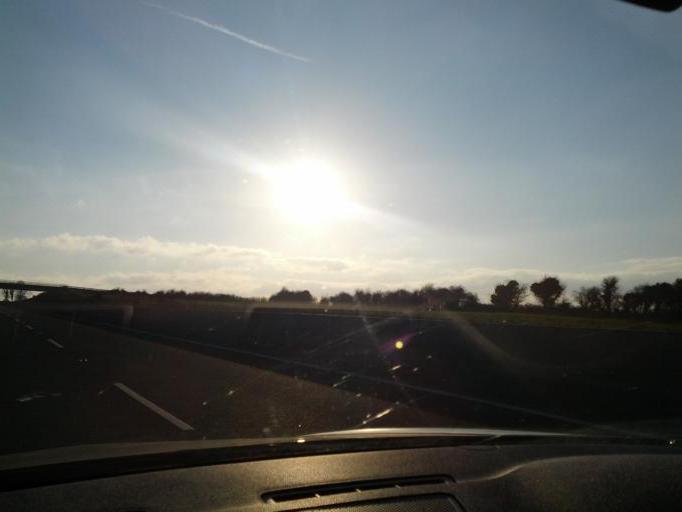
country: IE
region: Munster
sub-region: North Tipperary
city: Roscrea
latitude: 52.9026
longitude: -7.8986
